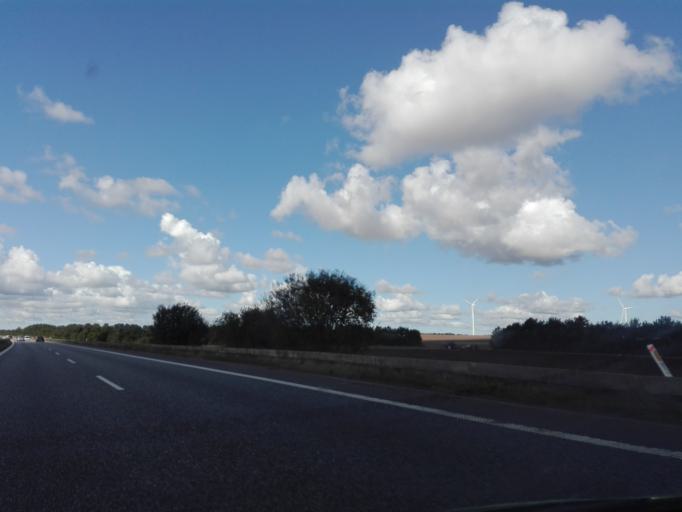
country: DK
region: Central Jutland
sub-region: Randers Kommune
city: Spentrup
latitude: 56.5167
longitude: 9.9619
